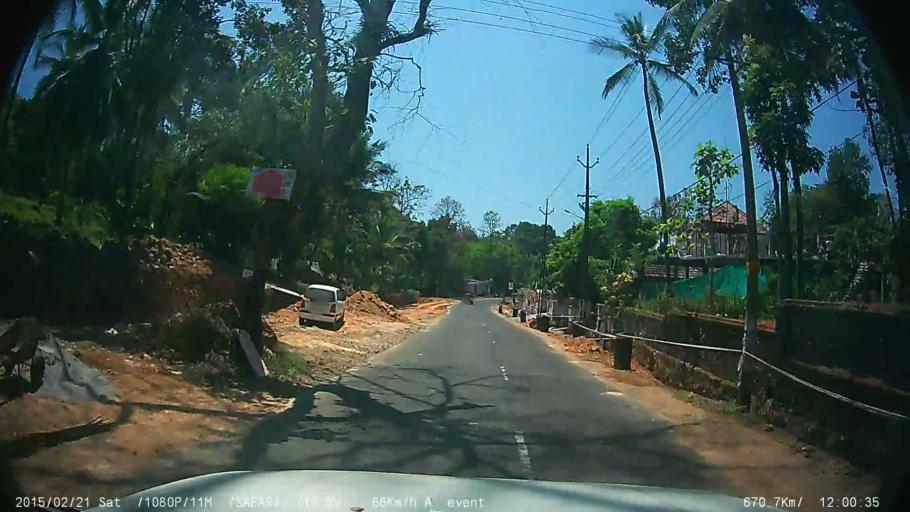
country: IN
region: Kerala
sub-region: Kottayam
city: Lalam
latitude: 9.7276
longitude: 76.6934
